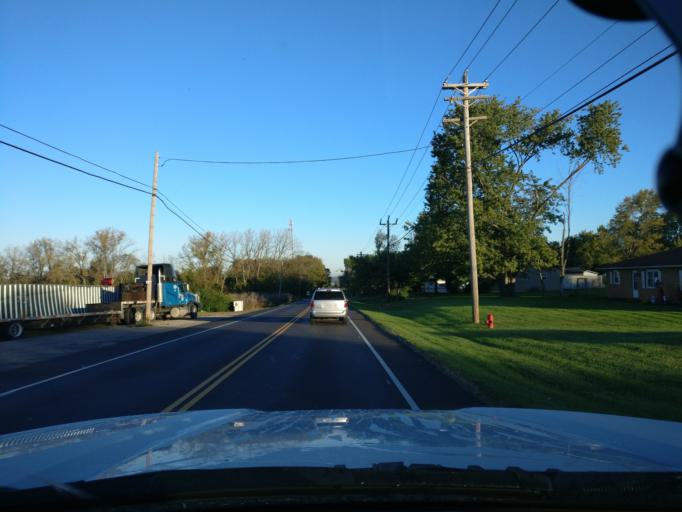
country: US
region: Ohio
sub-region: Warren County
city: Hunter
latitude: 39.5217
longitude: -84.2760
